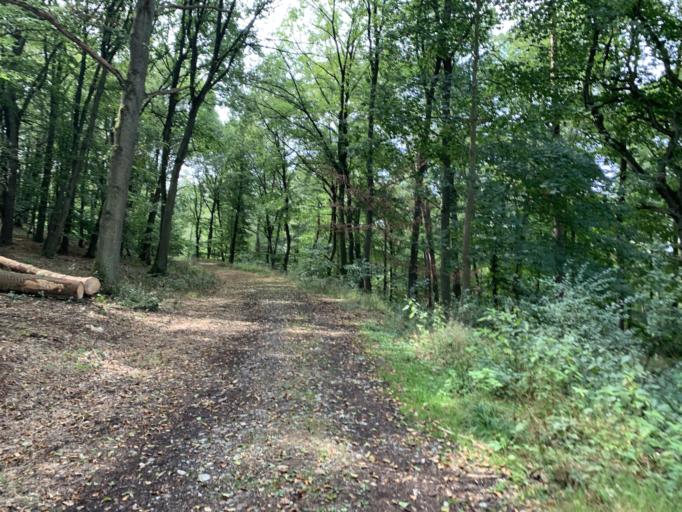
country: DE
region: Rheinland-Pfalz
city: Rettert
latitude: 50.2236
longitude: 7.9389
